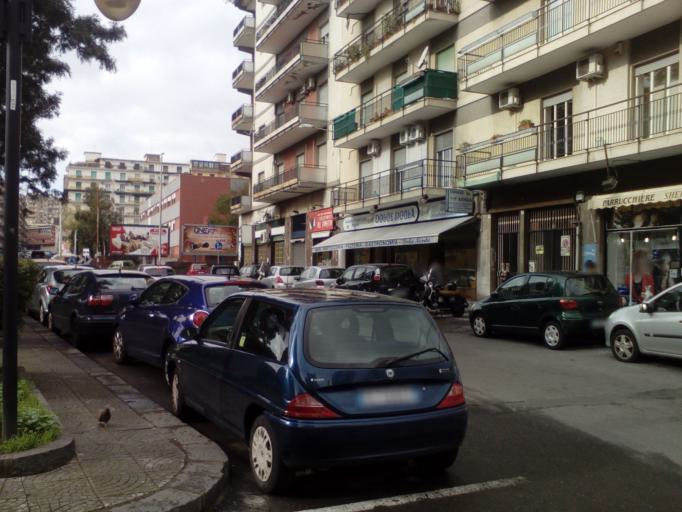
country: IT
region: Sicily
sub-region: Catania
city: Catania
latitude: 37.5162
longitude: 15.0802
